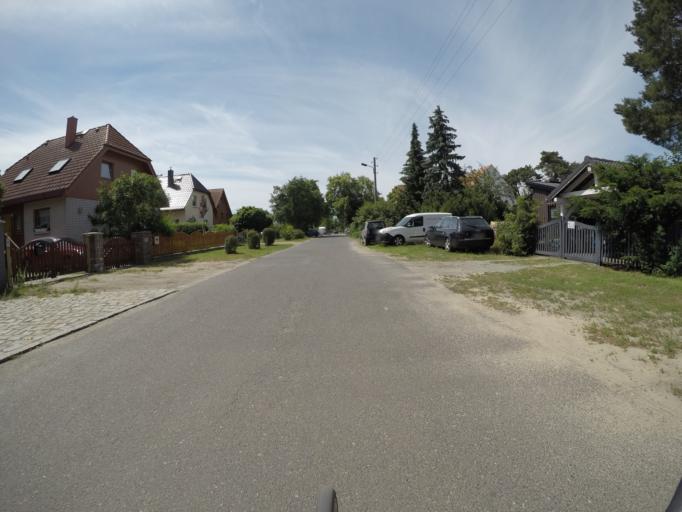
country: DE
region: Berlin
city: Mahlsdorf
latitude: 52.4857
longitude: 13.6169
